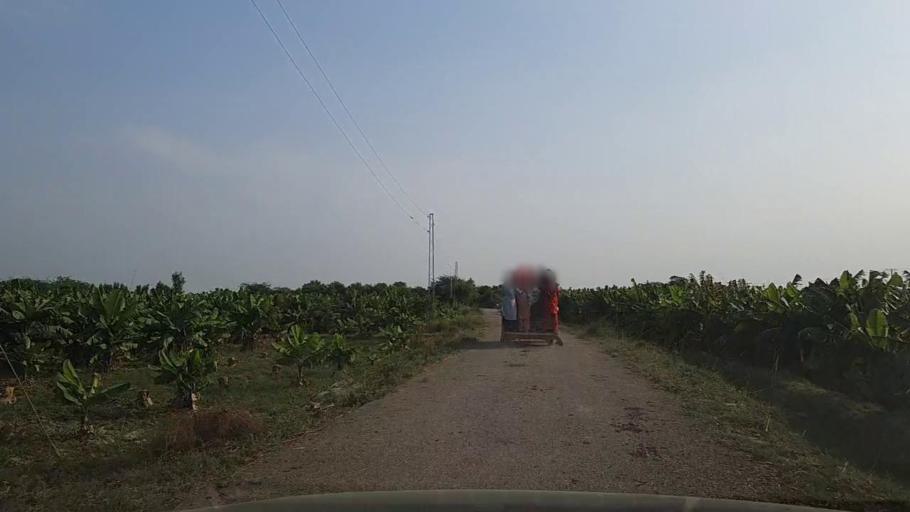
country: PK
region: Sindh
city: Thatta
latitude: 24.6417
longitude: 67.9509
